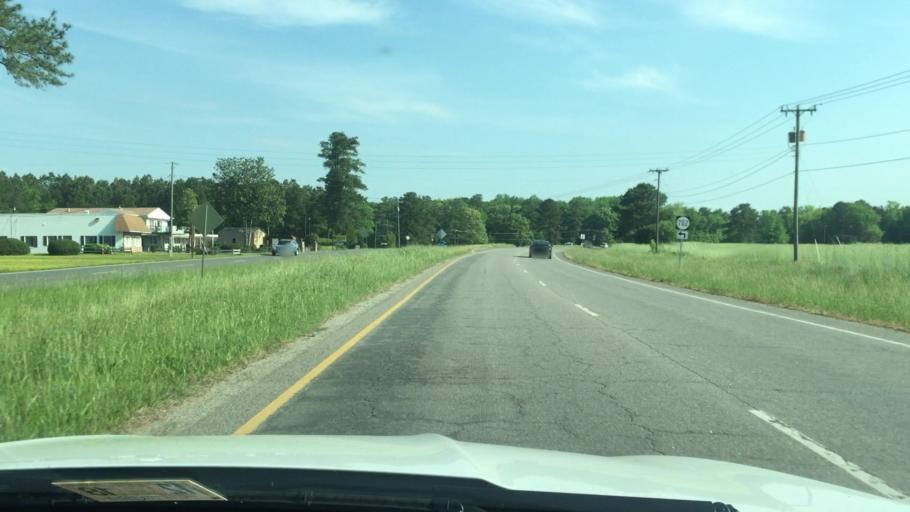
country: US
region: Virginia
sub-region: Lancaster County
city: Kilmarnock
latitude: 37.6560
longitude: -76.3886
